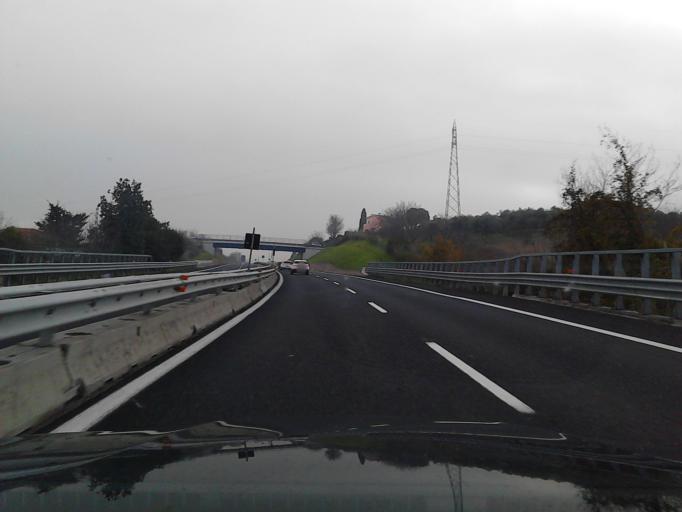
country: IT
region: Abruzzo
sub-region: Provincia di Pescara
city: San Martino Bassa
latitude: 42.5127
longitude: 14.1254
